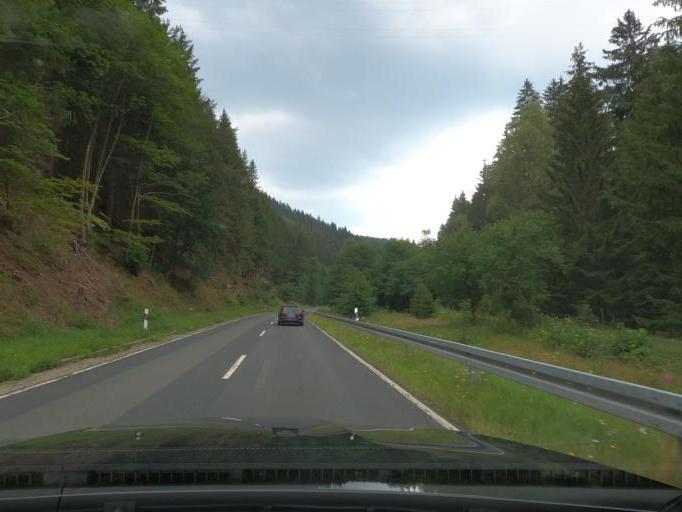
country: DE
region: Lower Saxony
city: Wildemann
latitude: 51.8450
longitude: 10.2677
